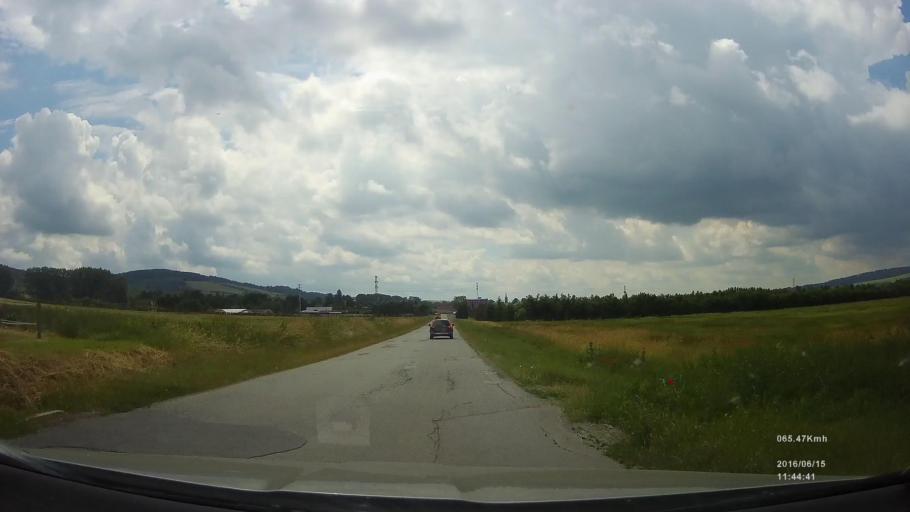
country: SK
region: Kosicky
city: Kosice
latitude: 48.7422
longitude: 21.3455
